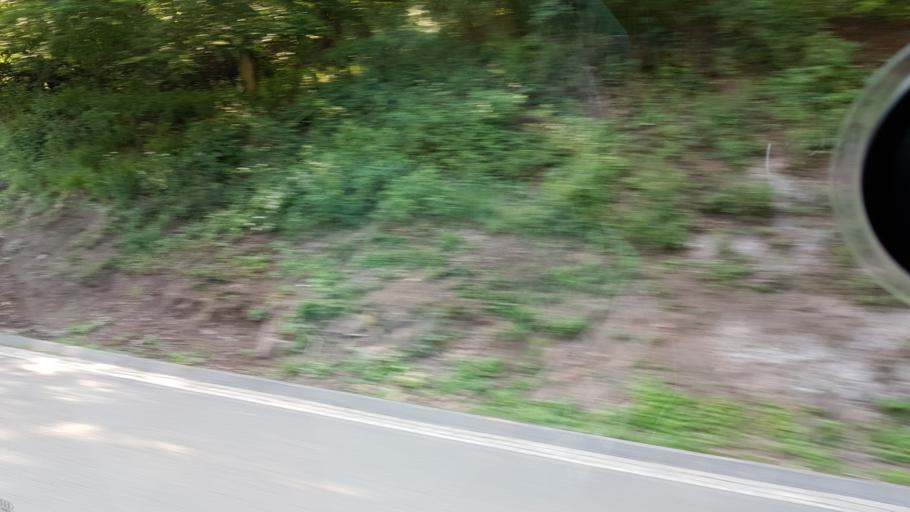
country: DE
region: Rheinland-Pfalz
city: Oberalben
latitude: 49.6023
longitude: 7.4133
